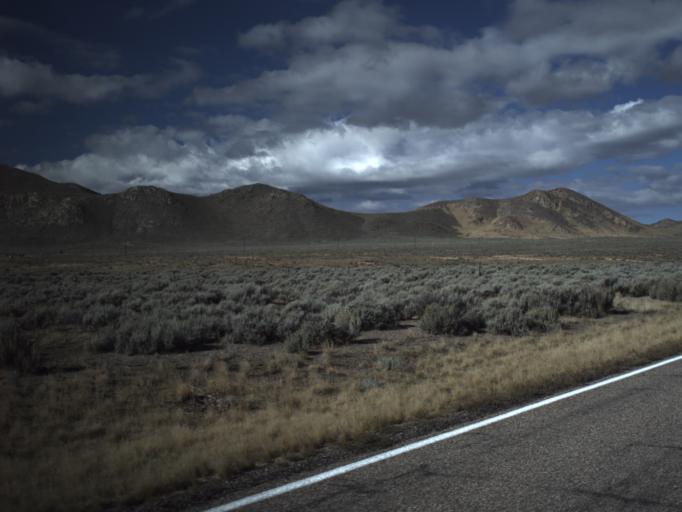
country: US
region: Utah
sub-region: Beaver County
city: Milford
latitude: 38.4158
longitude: -113.0822
